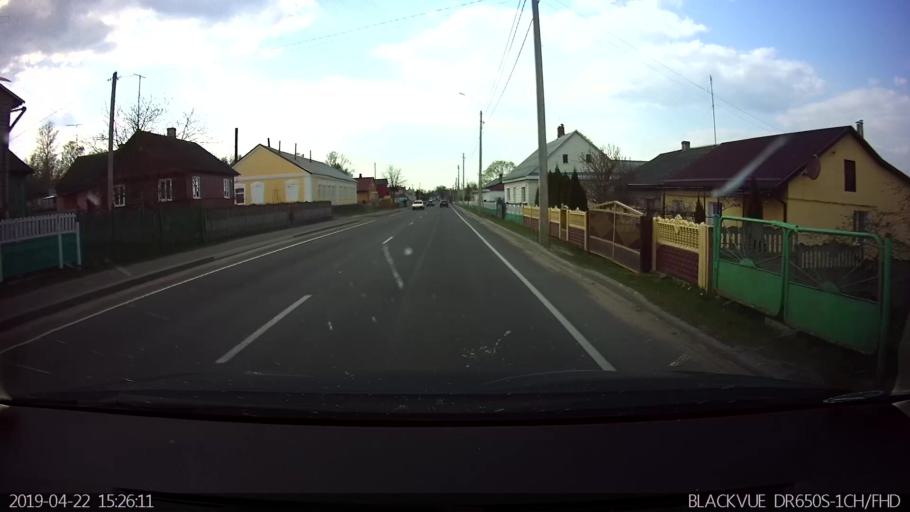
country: BY
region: Brest
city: Vysokaye
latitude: 52.3671
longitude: 23.3851
